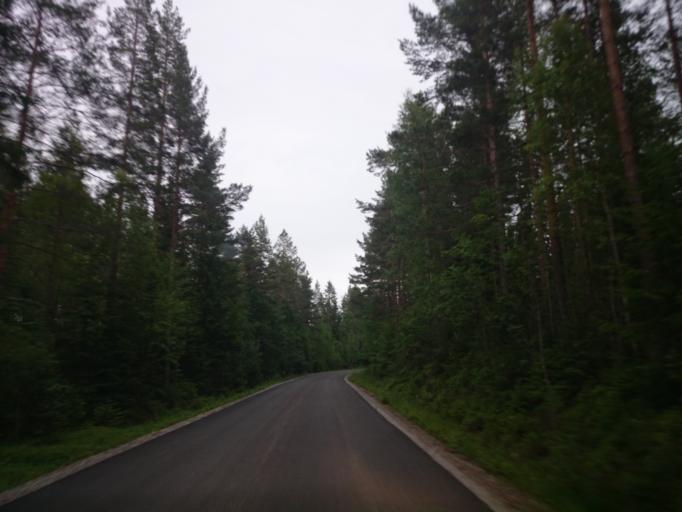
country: SE
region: Vaesternorrland
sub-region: Sundsvalls Kommun
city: Njurundabommen
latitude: 62.1273
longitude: 17.4195
